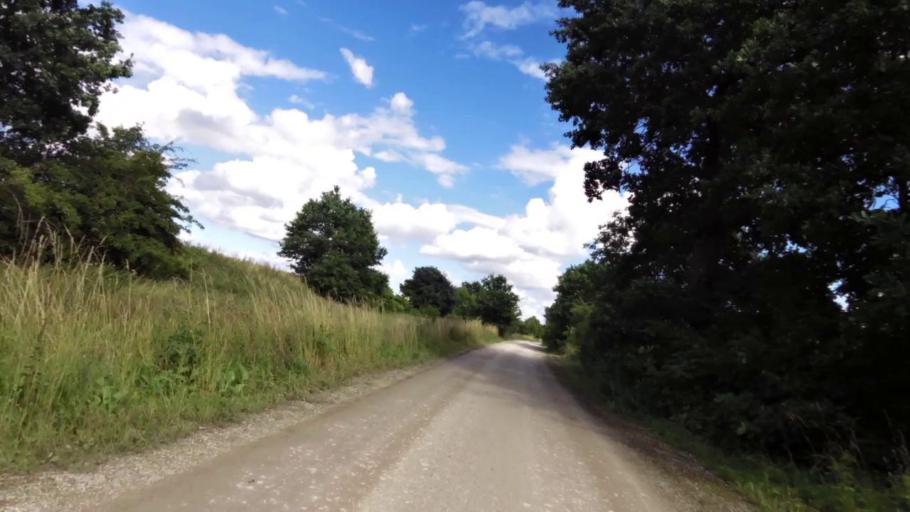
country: PL
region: Pomeranian Voivodeship
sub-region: Powiat slupski
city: Ustka
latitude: 54.5166
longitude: 16.7222
